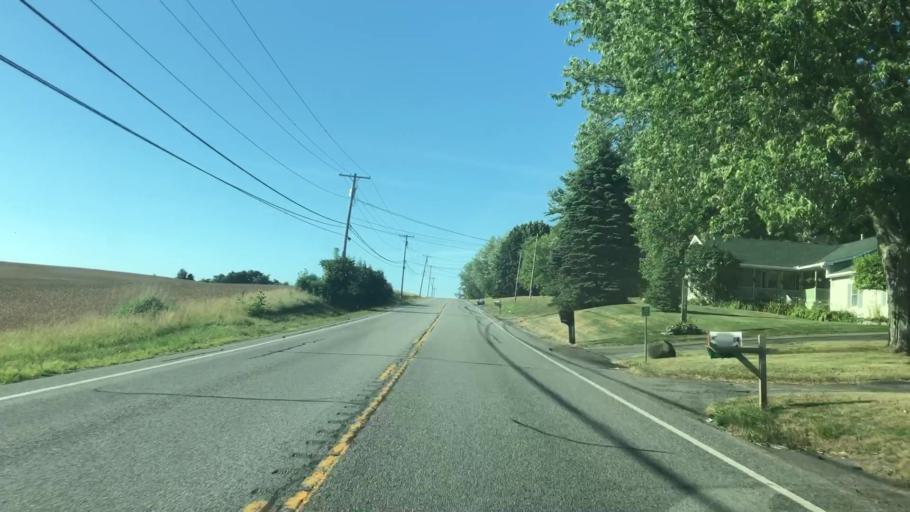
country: US
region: New York
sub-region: Wayne County
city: Macedon
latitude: 43.1343
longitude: -77.2926
